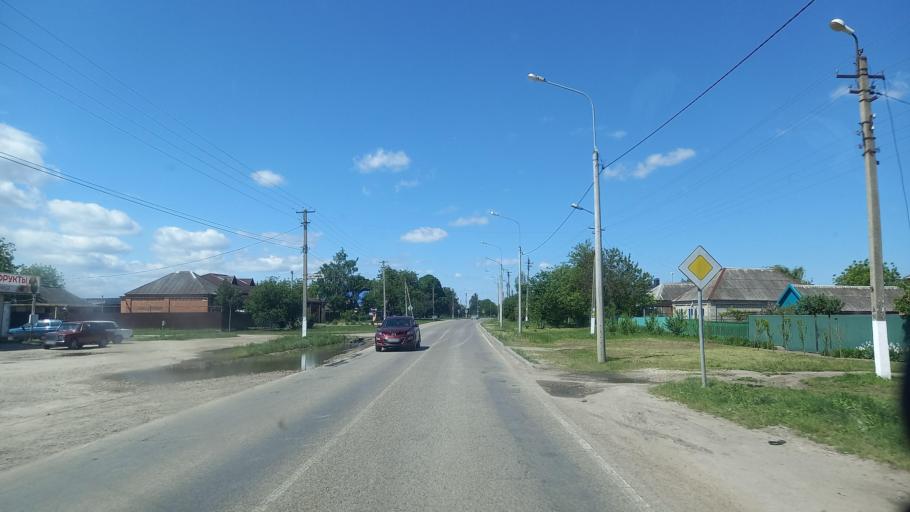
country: RU
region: Krasnodarskiy
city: Novoukrainskoye
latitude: 45.3802
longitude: 40.5388
